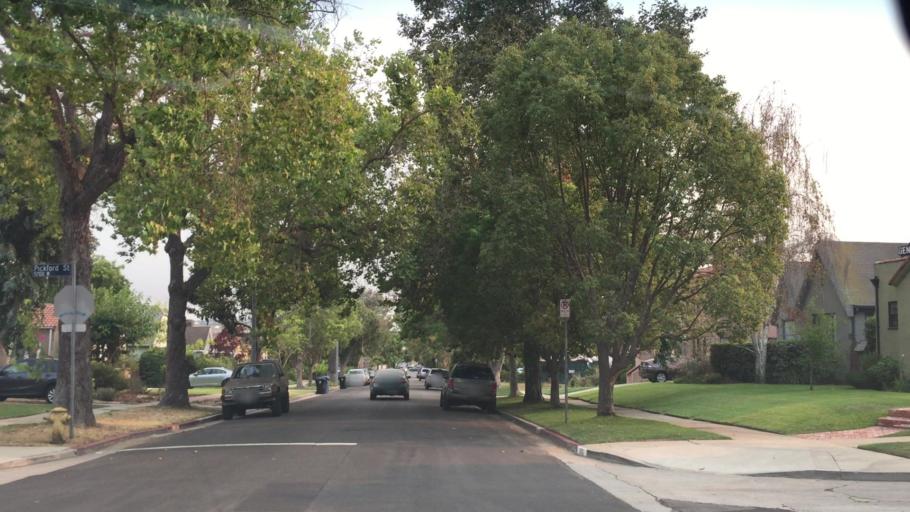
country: US
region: California
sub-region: Los Angeles County
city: Culver City
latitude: 34.0471
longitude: -118.3646
